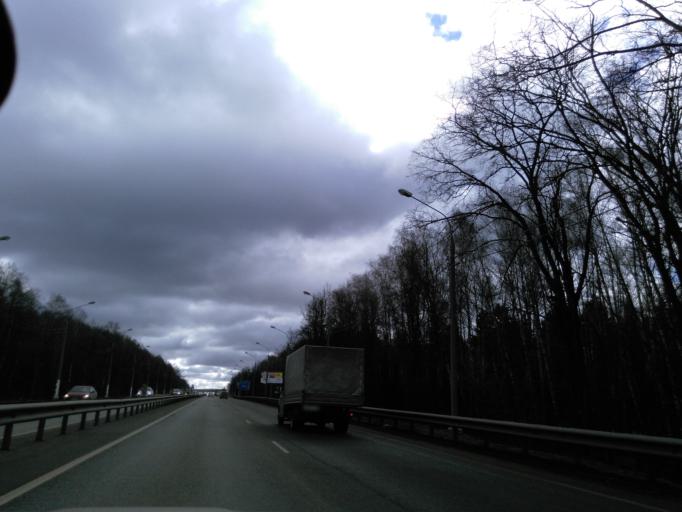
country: RU
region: Moskovskaya
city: Mendeleyevo
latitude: 56.0128
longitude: 37.2114
